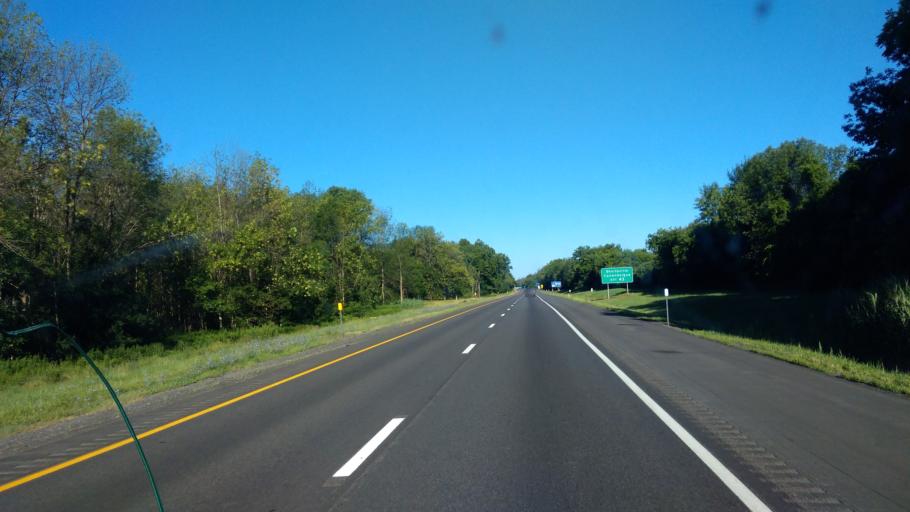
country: US
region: New York
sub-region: Ontario County
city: Manchester
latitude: 42.9775
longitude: -77.2046
